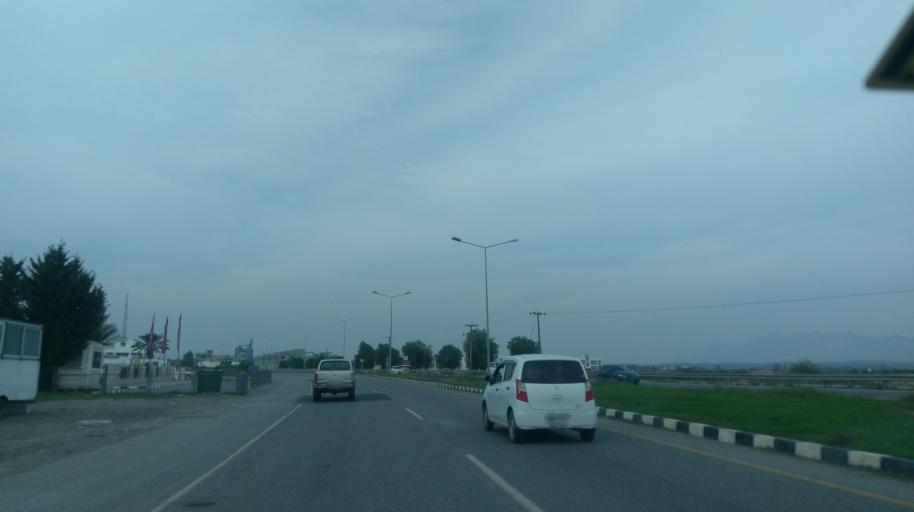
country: CY
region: Lefkosia
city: Mammari
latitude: 35.2128
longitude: 33.2786
